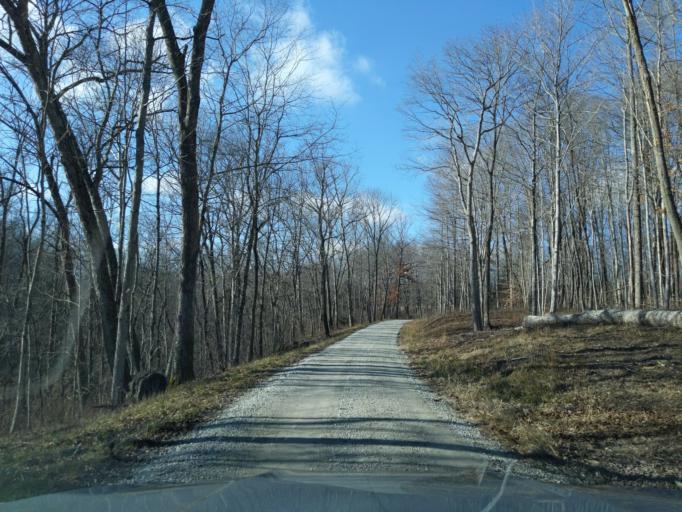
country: US
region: Indiana
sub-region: Decatur County
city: Greensburg
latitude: 39.2399
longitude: -85.4827
